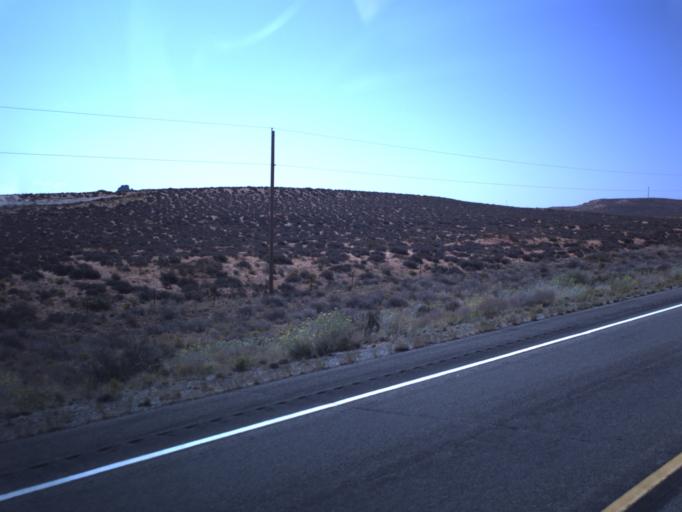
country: US
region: Utah
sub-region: San Juan County
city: Blanding
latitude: 37.0570
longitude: -109.5664
